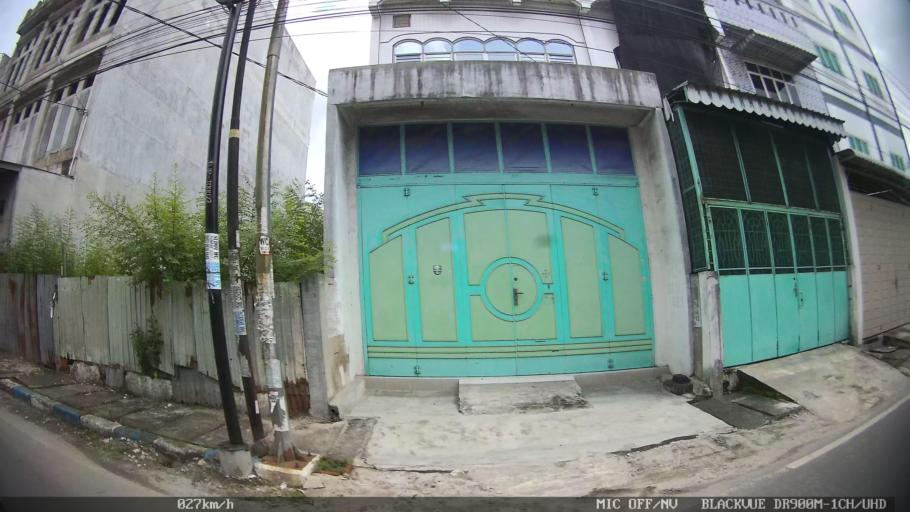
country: ID
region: North Sumatra
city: Percut
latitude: 3.5637
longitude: 98.8751
